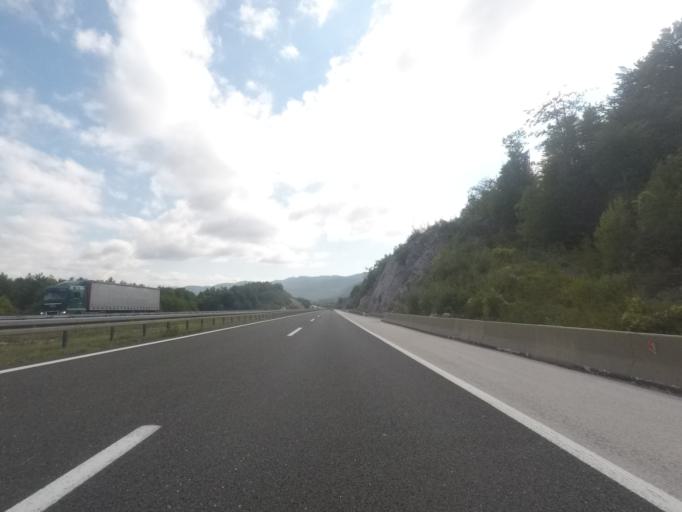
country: HR
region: Zadarska
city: Obrovac
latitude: 44.3609
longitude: 15.6395
